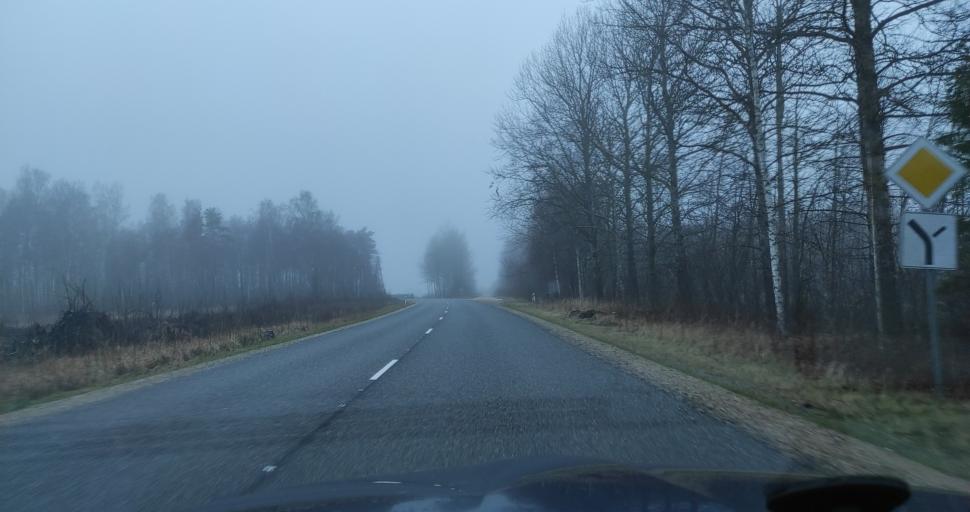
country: LV
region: Alsunga
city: Alsunga
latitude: 56.9948
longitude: 21.3711
